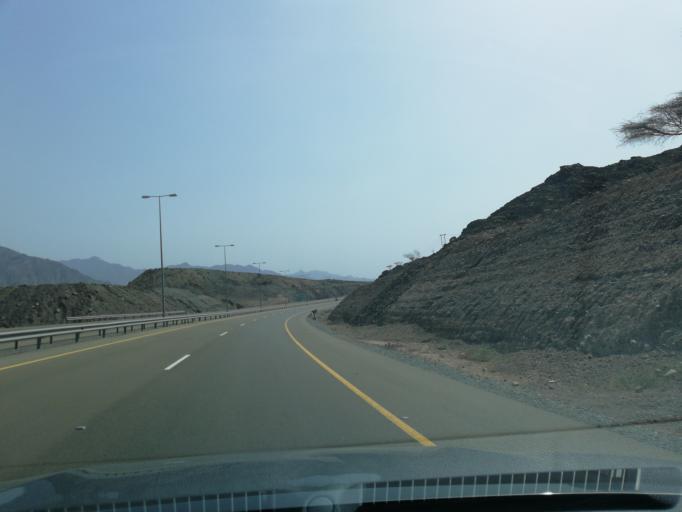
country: OM
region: Al Batinah
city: Al Liwa'
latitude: 24.2297
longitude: 56.3369
